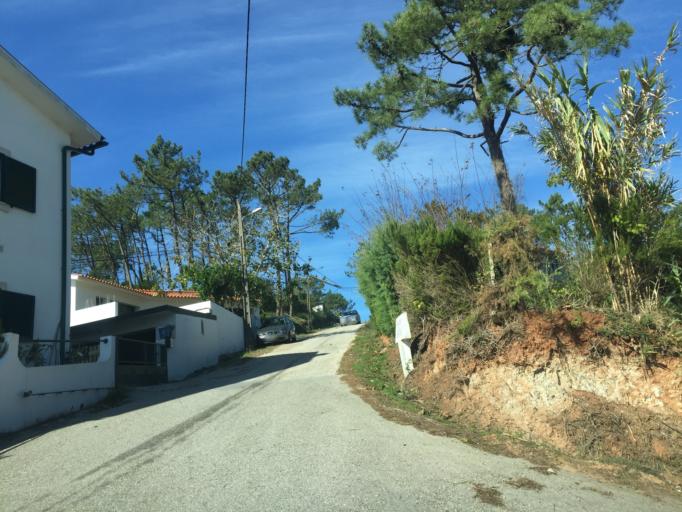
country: PT
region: Coimbra
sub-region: Figueira da Foz
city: Tavarede
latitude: 40.1844
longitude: -8.8380
